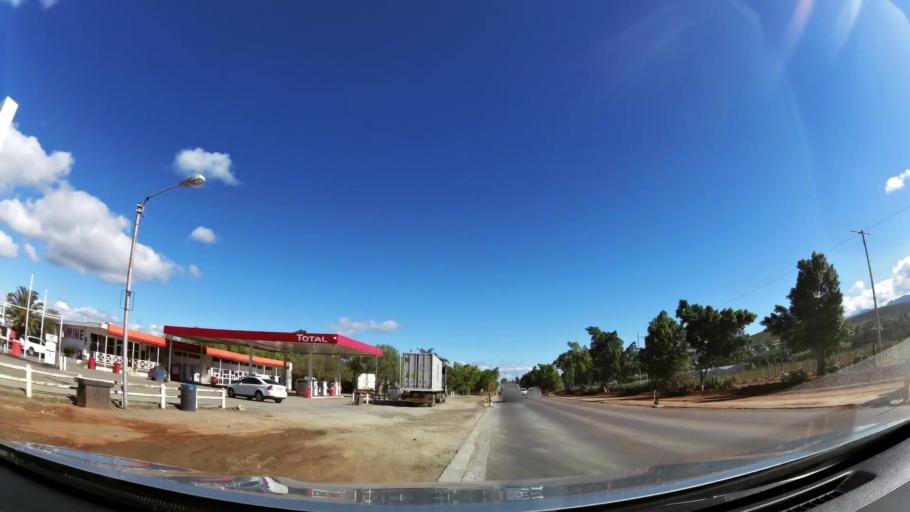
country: ZA
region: Western Cape
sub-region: Cape Winelands District Municipality
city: Ashton
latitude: -33.8322
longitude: 20.0704
